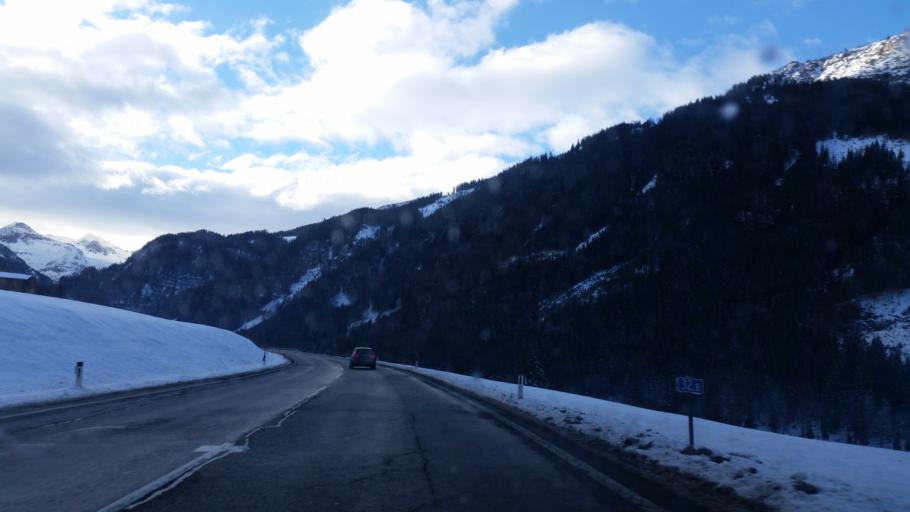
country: AT
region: Salzburg
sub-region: Politischer Bezirk Sankt Johann im Pongau
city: Untertauern
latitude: 47.3139
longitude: 13.5090
